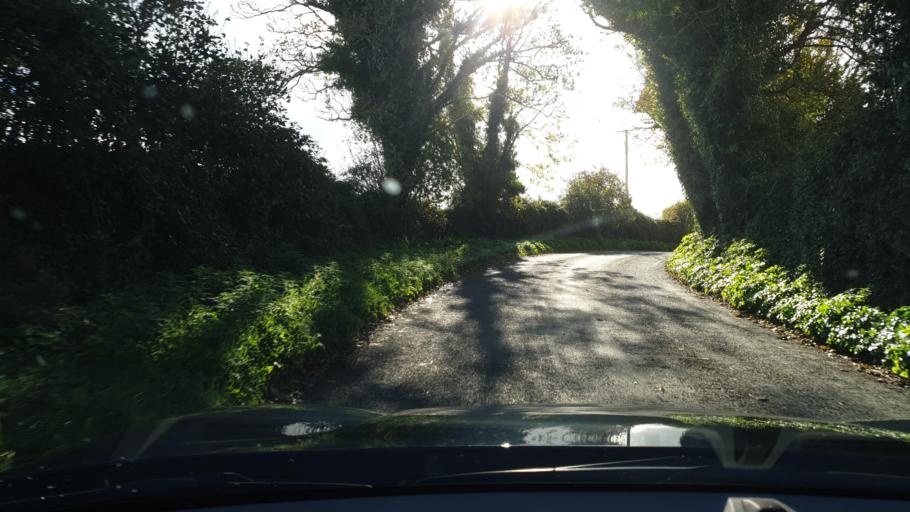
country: IE
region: Leinster
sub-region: Fingal County
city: Skerries
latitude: 53.5672
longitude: -6.1097
